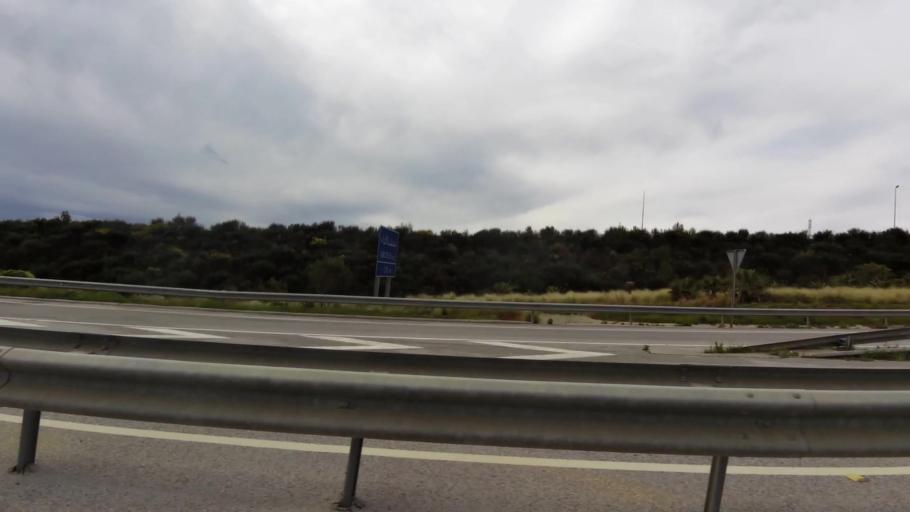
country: ES
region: Ceuta
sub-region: Ceuta
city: Ceuta
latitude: 35.7482
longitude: -5.3506
